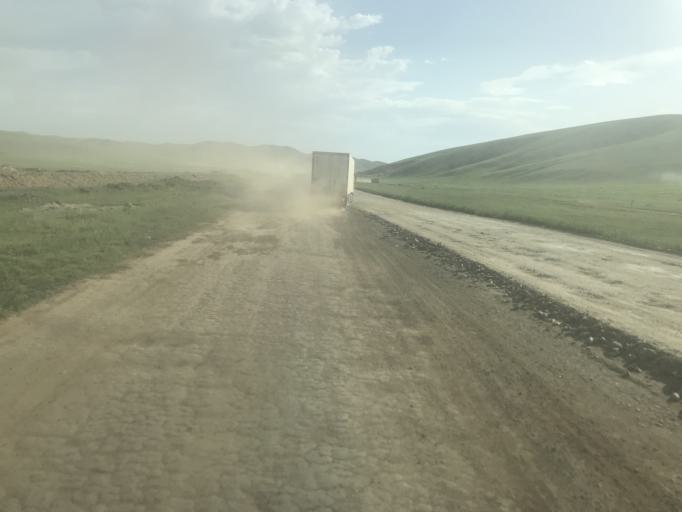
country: MN
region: Central Aimak
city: Bornuur
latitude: 48.6766
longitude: 106.1432
